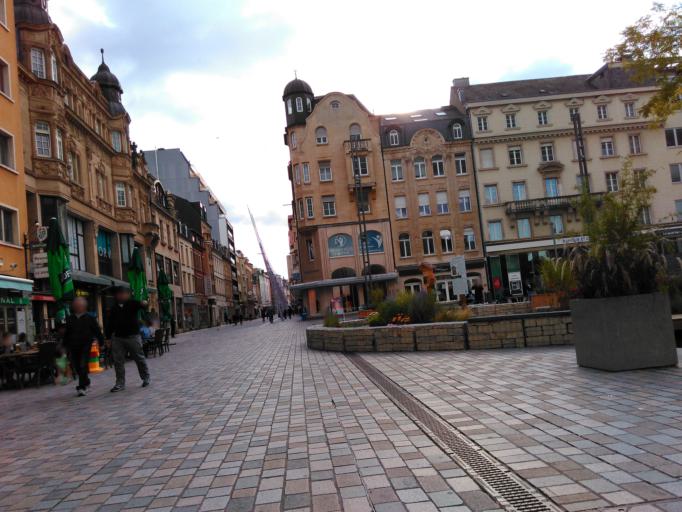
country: LU
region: Luxembourg
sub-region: Canton d'Esch-sur-Alzette
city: Esch-sur-Alzette
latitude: 49.4959
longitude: 5.9853
